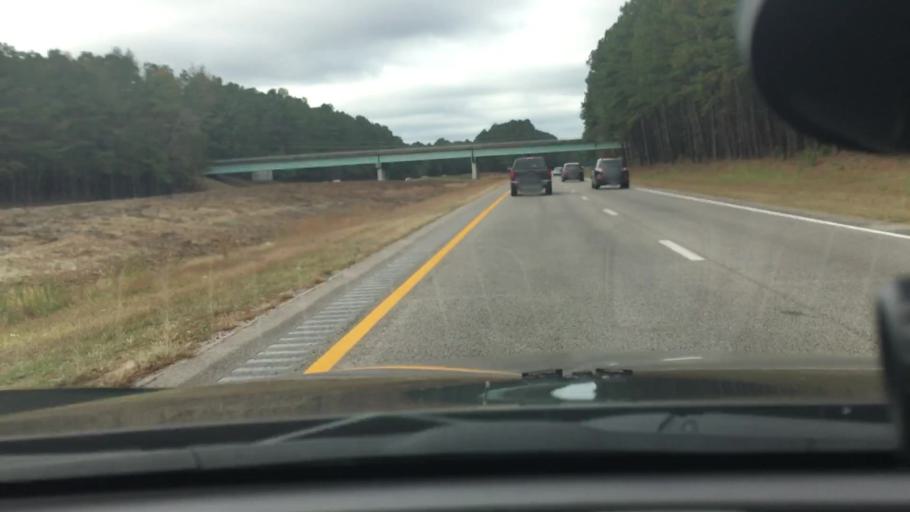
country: US
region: North Carolina
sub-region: Nash County
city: Spring Hope
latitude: 35.7894
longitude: -78.1361
